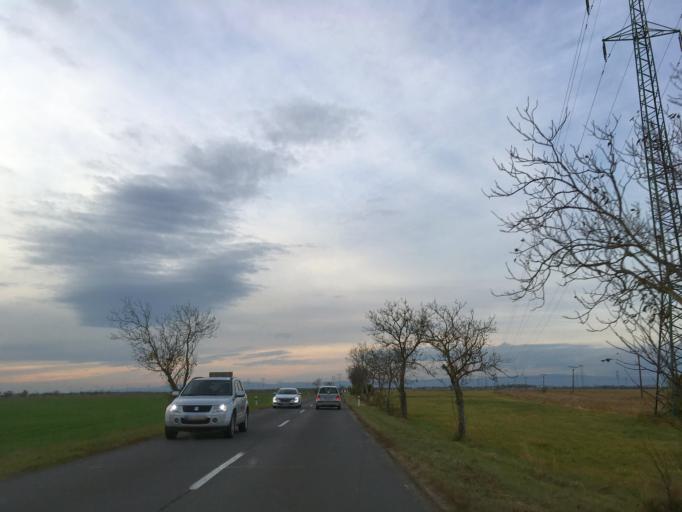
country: SK
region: Bratislavsky
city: Dunajska Luzna
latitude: 48.1133
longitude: 17.3179
